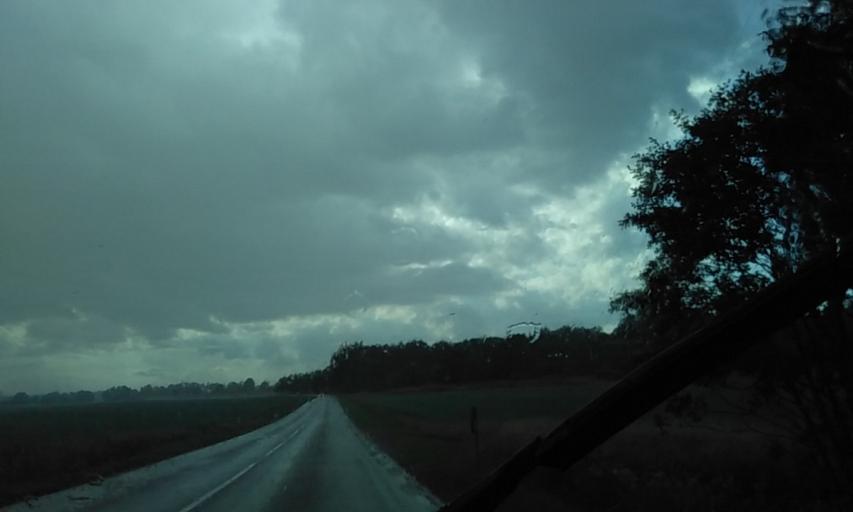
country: SE
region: Vaestra Goetaland
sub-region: Lidkopings Kommun
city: Lidkoping
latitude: 58.5032
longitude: 12.9462
